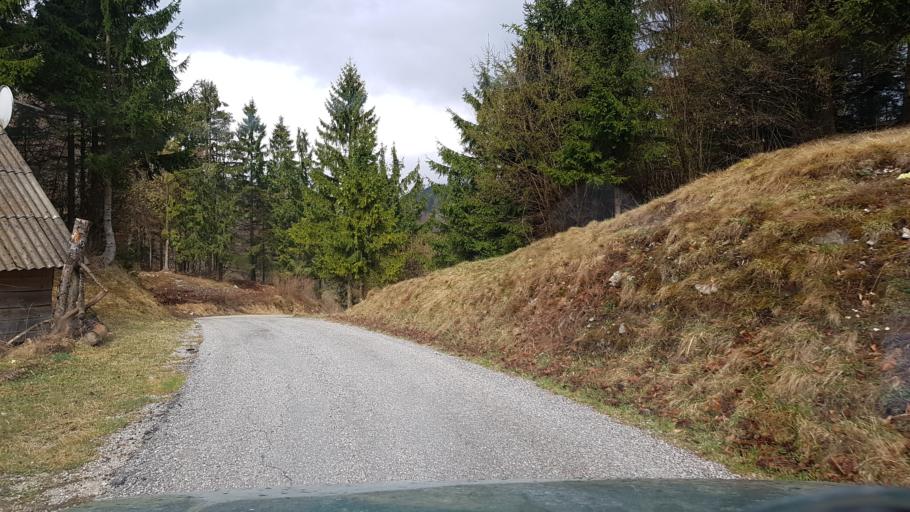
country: SI
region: Cerkno
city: Cerkno
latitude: 46.1389
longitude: 13.8805
